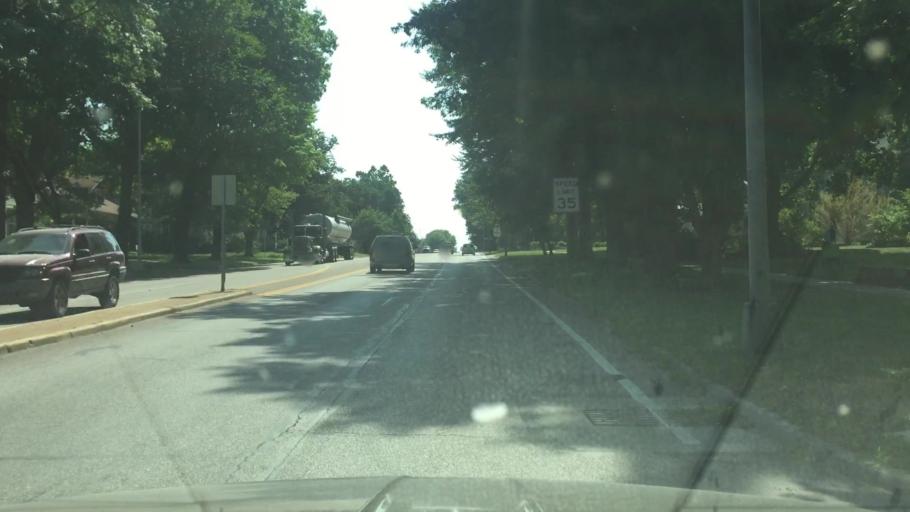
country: US
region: Missouri
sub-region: Pettis County
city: Sedalia
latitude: 38.7044
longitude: -93.2363
